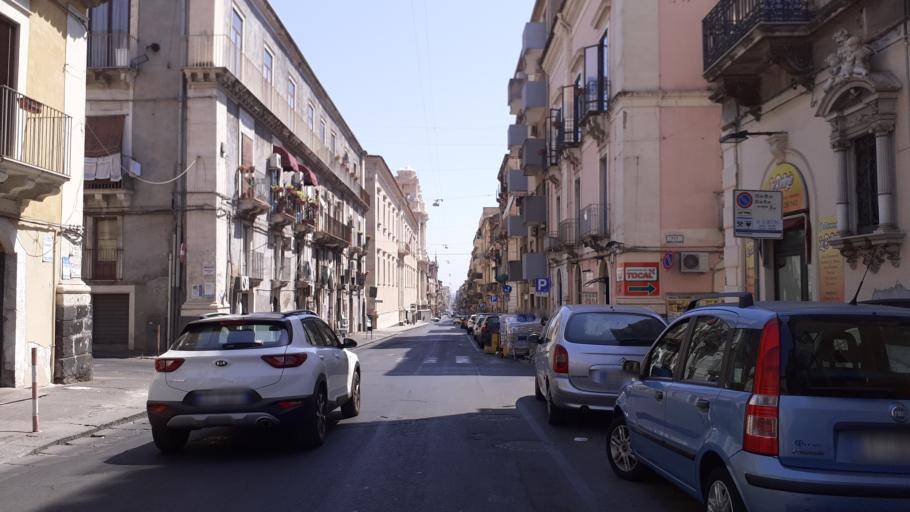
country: IT
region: Sicily
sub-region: Catania
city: Catania
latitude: 37.5019
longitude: 15.0790
